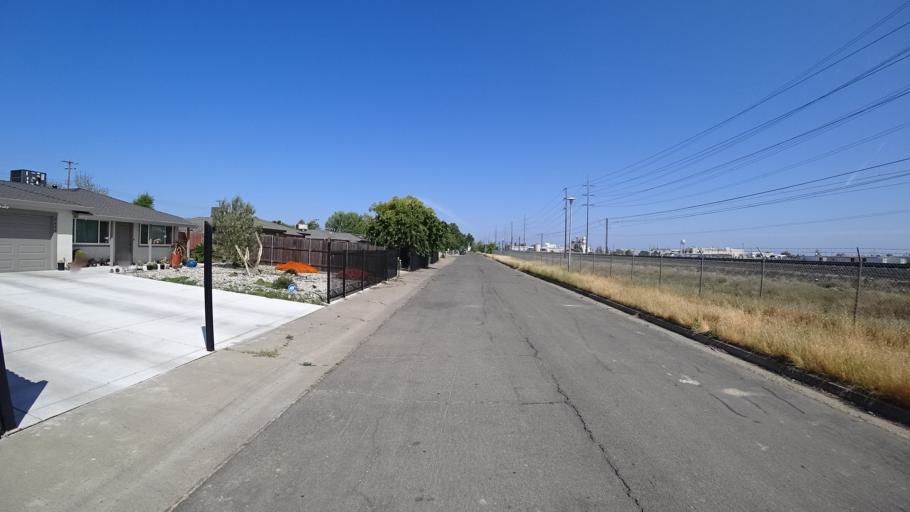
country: US
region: California
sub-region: Sacramento County
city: Parkway
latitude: 38.5051
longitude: -121.4741
